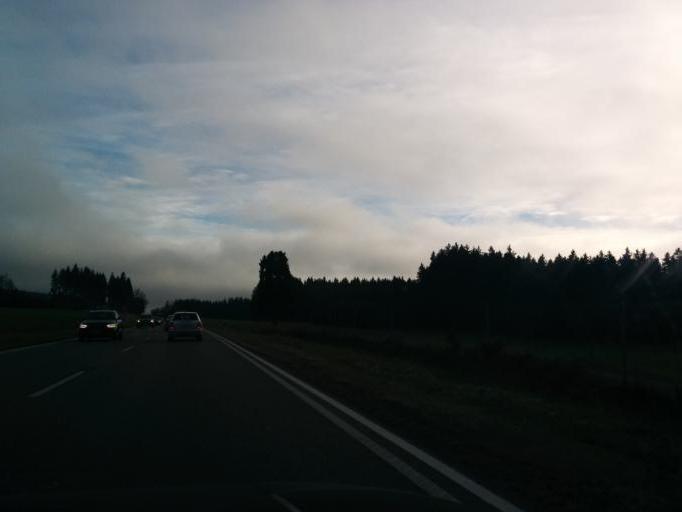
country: DE
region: Bavaria
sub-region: Swabia
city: Mauerstetten
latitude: 47.8595
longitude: 10.6582
